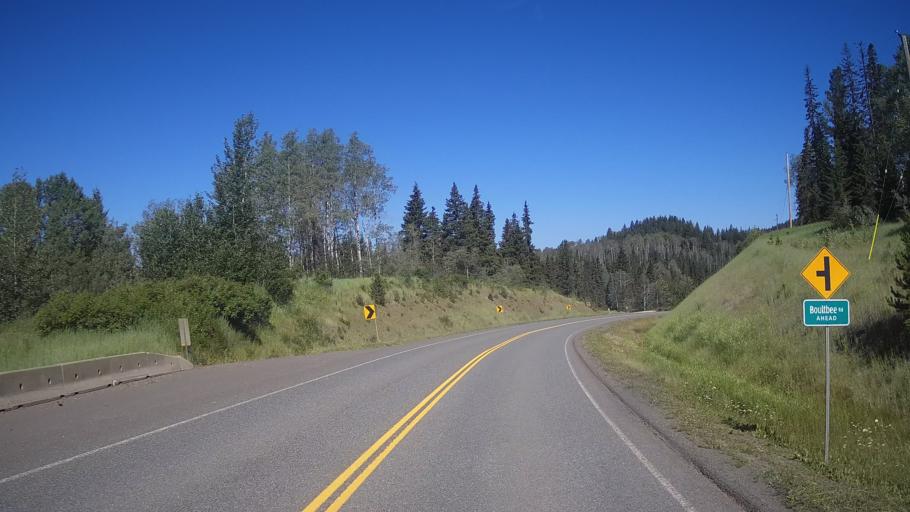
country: CA
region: British Columbia
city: Kamloops
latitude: 51.4999
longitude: -120.5978
